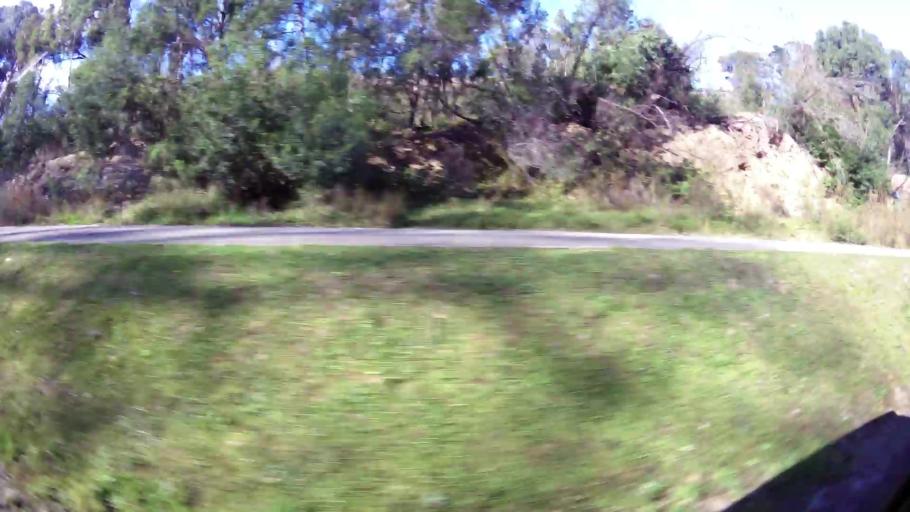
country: ZA
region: Western Cape
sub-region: Eden District Municipality
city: Knysna
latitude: -34.0303
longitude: 23.0489
